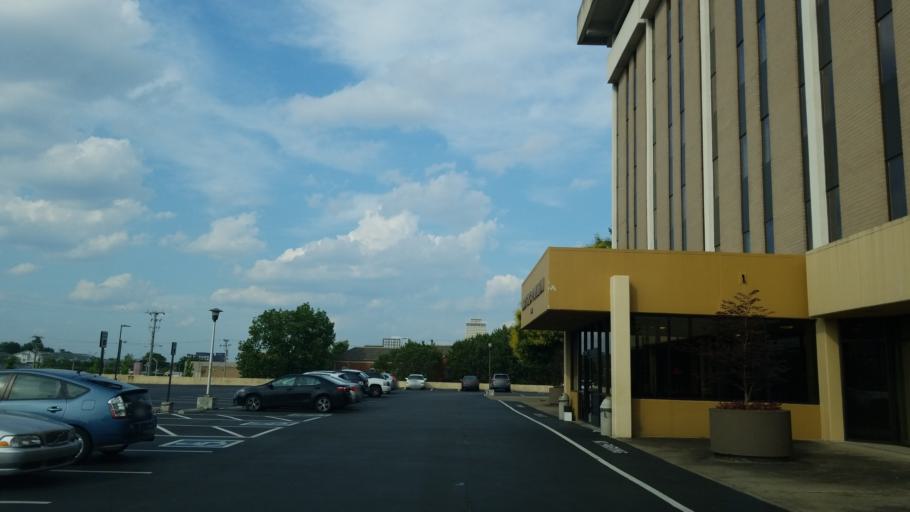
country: US
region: Tennessee
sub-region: Davidson County
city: Nashville
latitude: 36.1558
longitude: -86.8023
